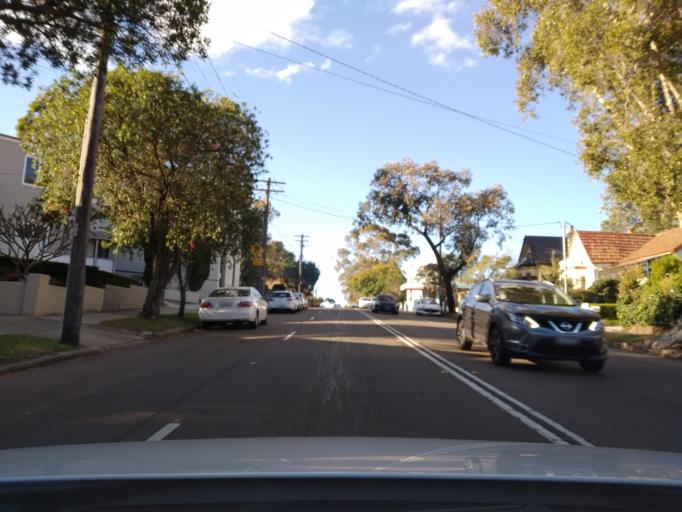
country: AU
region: New South Wales
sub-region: Ashfield
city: Summer Hill
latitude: -33.8969
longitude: 151.1368
